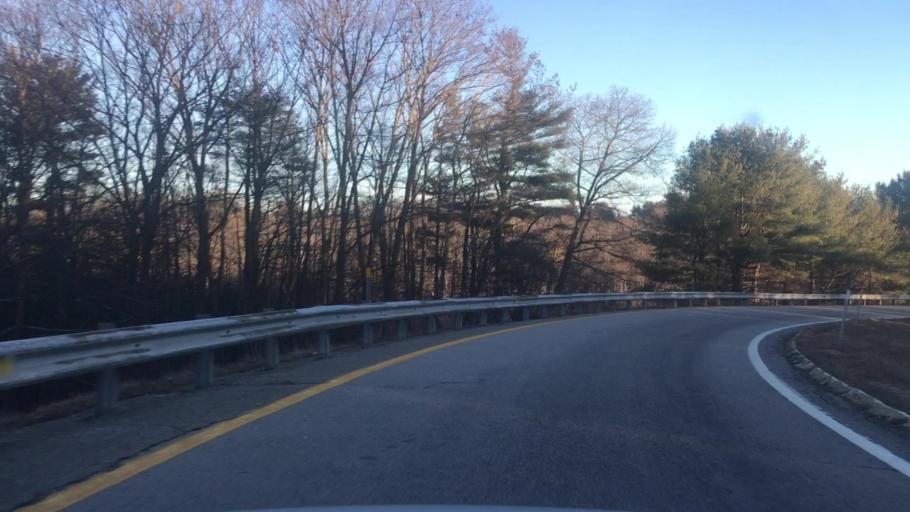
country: US
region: Maine
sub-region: York County
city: Kittery
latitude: 43.0988
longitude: -70.7541
